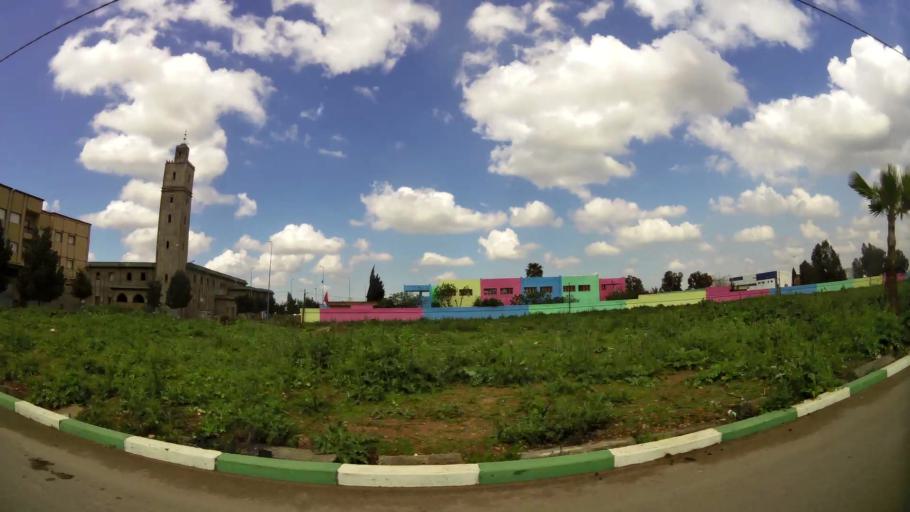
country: MA
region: Grand Casablanca
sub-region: Mediouna
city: Mediouna
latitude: 33.3882
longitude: -7.5422
